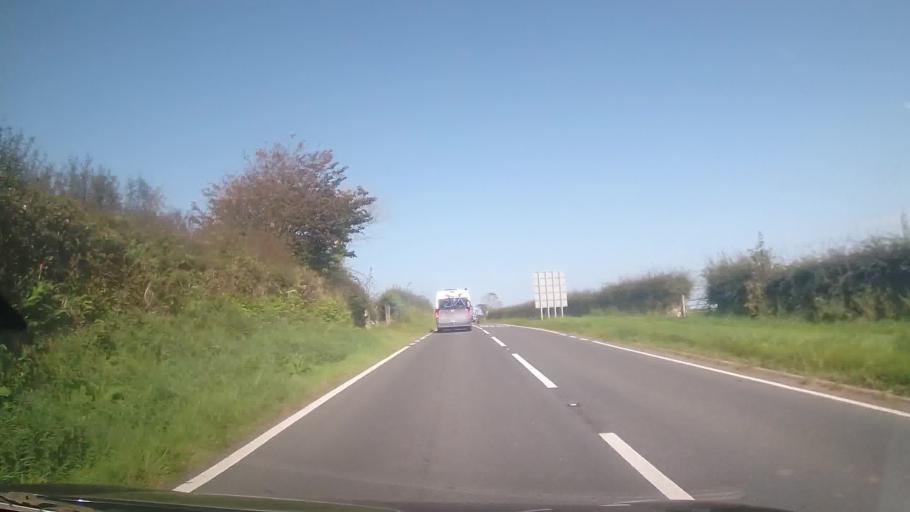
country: GB
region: Wales
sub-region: County of Ceredigion
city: Cardigan
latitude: 52.0552
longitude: -4.6898
